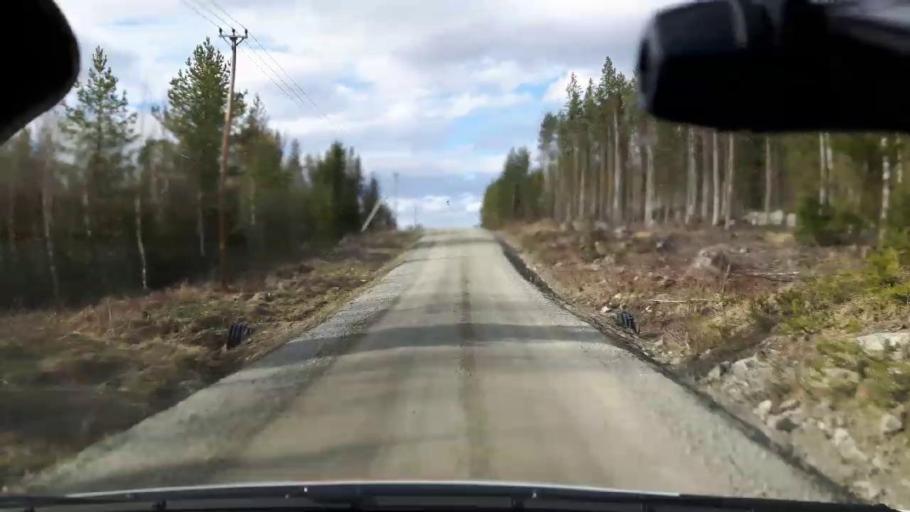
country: SE
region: Jaemtland
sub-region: Bergs Kommun
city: Hoverberg
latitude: 62.8743
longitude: 14.6667
